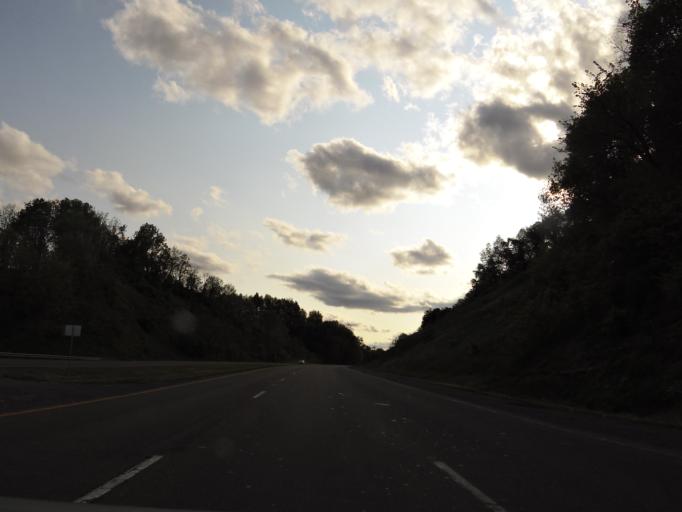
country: US
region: Virginia
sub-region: Tazewell County
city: Tazewell
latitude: 37.1204
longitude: -81.5500
